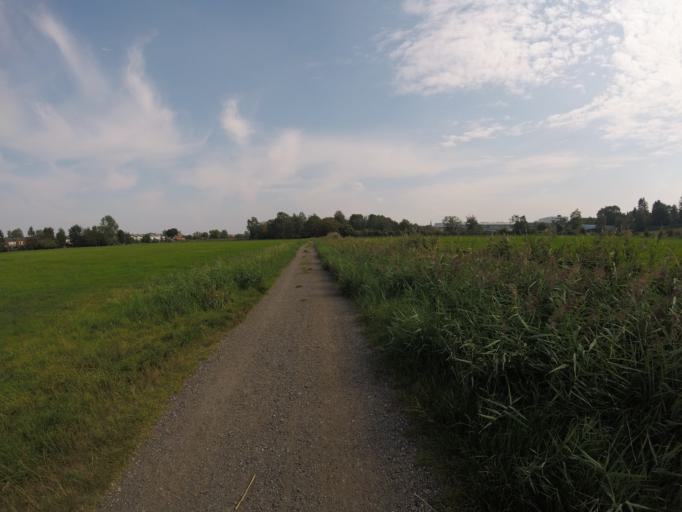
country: DE
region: Lower Saxony
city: Stade
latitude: 53.6110
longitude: 9.4639
